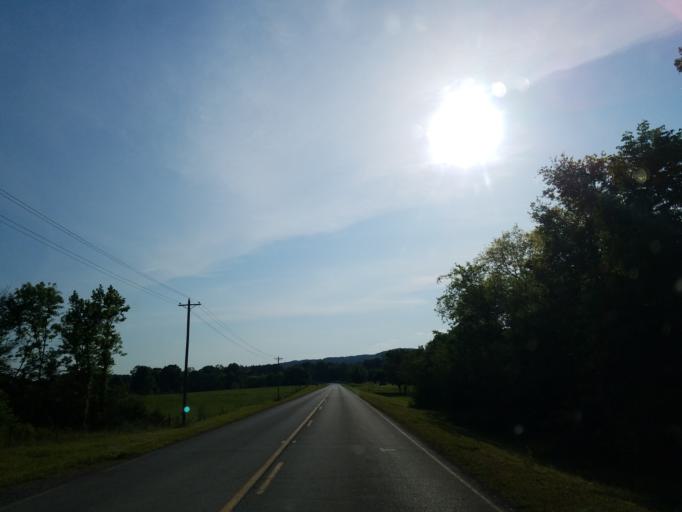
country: US
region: Georgia
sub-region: Chattooga County
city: Trion
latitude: 34.5637
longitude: -85.1769
